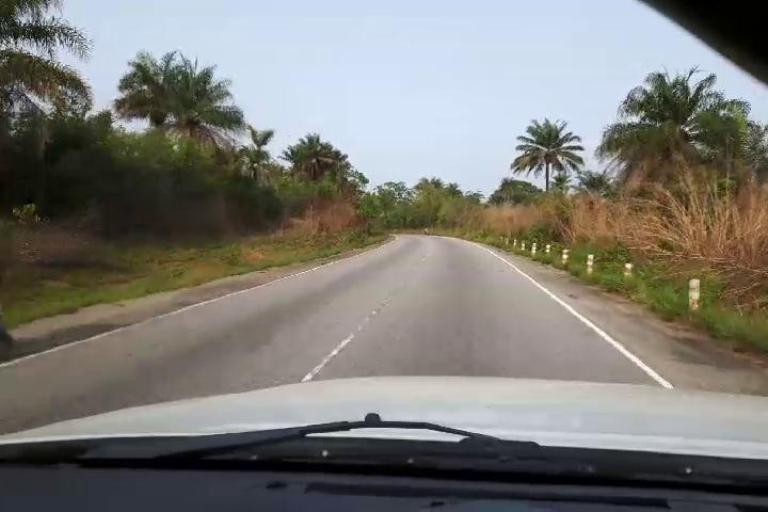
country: SL
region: Southern Province
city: Baoma
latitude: 7.9268
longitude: -11.5339
